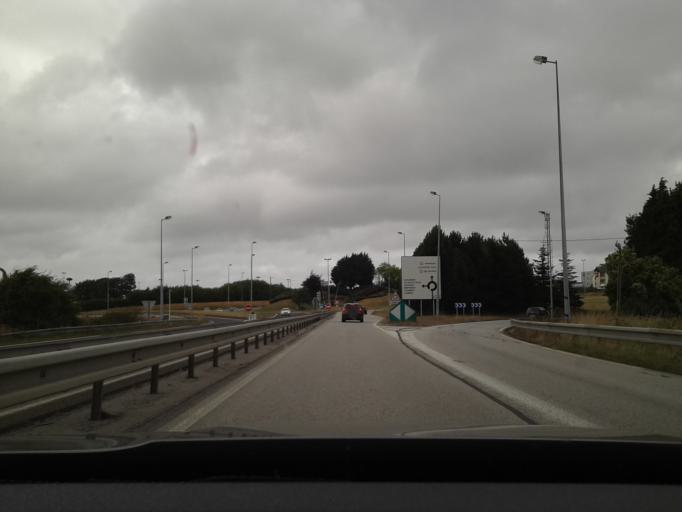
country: FR
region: Lower Normandy
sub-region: Departement de la Manche
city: La Glacerie
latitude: 49.5978
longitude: -1.5968
